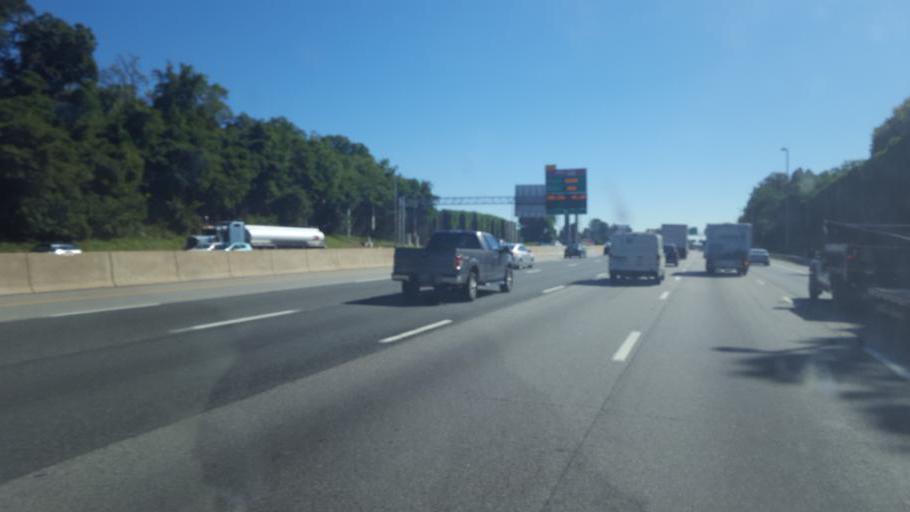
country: US
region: Virginia
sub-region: Fairfax County
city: North Springfield
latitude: 38.7981
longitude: -77.1990
